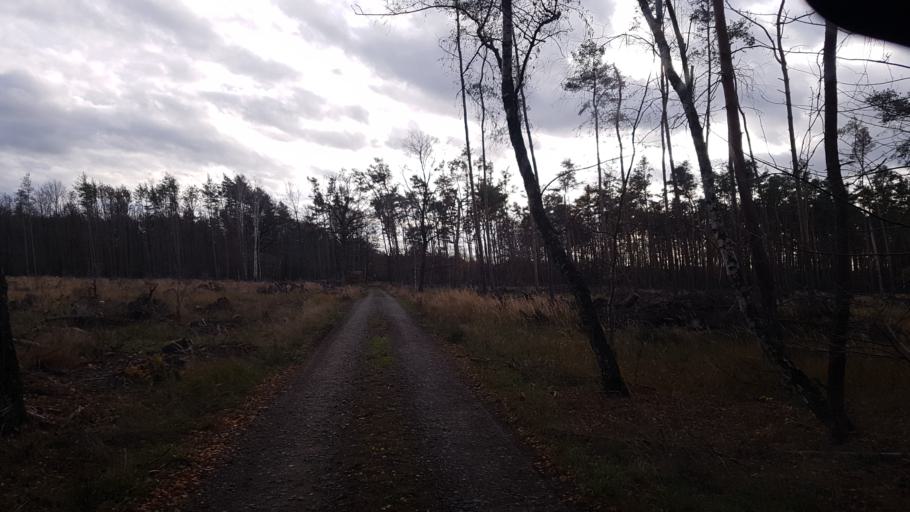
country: DE
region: Brandenburg
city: Falkenberg
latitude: 51.5679
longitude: 13.2833
